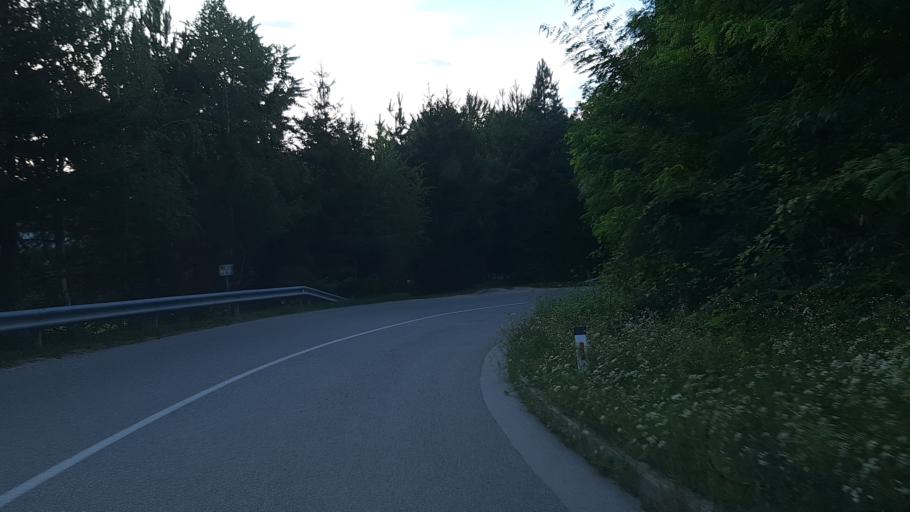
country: SI
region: Dobje
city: Dobje pri Planini
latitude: 46.1417
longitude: 15.4468
